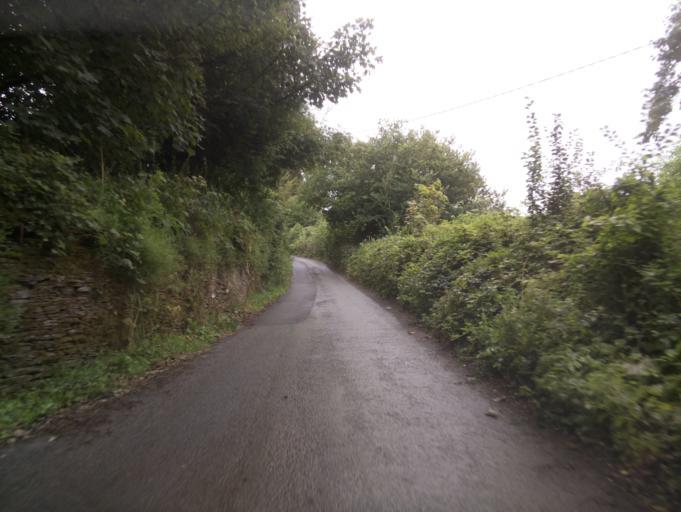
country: GB
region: England
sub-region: Devon
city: Kingsbridge
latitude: 50.3212
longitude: -3.7143
